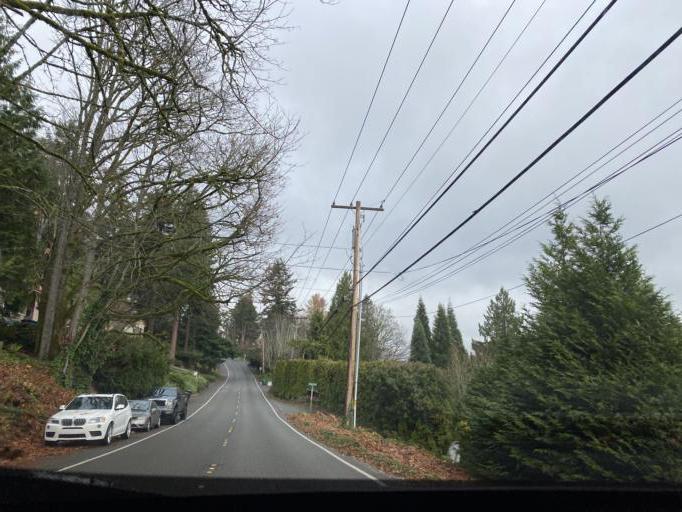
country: US
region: Washington
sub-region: King County
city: Mercer Island
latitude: 47.5362
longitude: -122.2134
